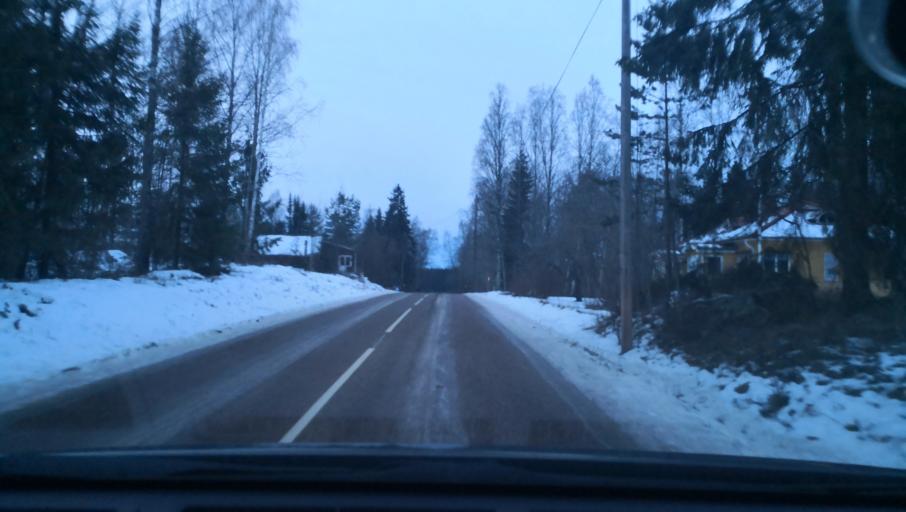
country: SE
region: Dalarna
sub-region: Avesta Kommun
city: Horndal
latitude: 60.1945
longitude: 16.4652
